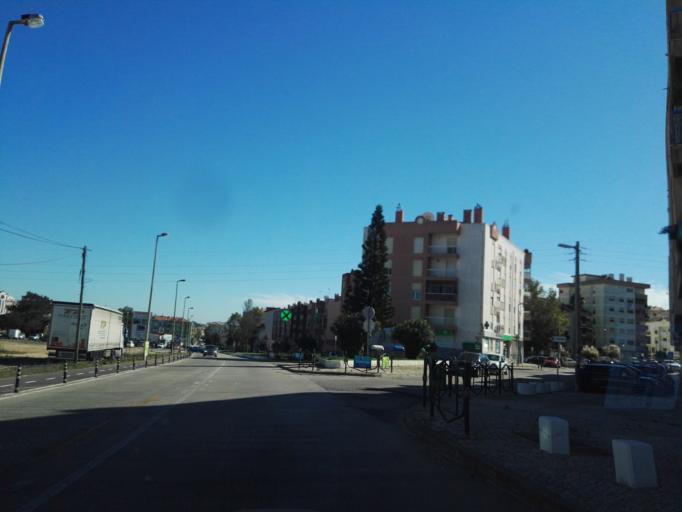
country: PT
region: Lisbon
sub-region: Sintra
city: Sintra
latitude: 38.7992
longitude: -9.3557
